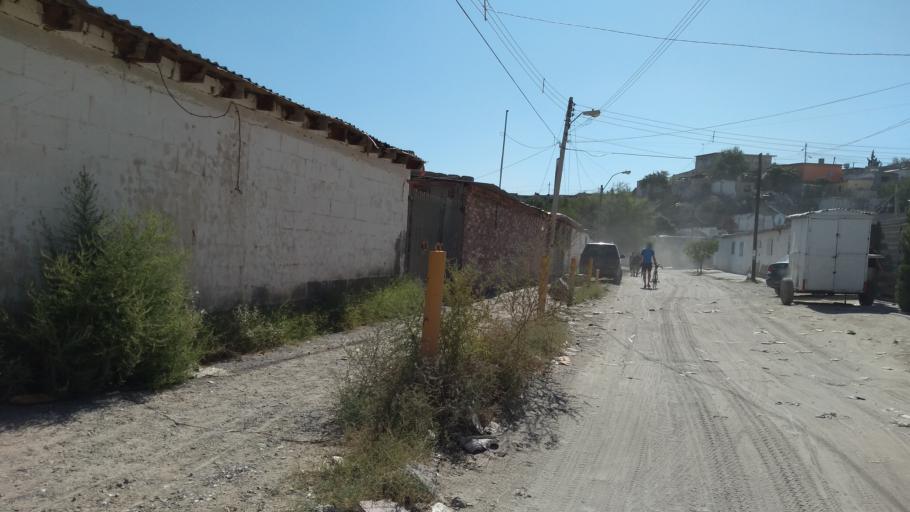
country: US
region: Texas
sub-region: El Paso County
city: El Paso
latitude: 31.7599
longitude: -106.5096
